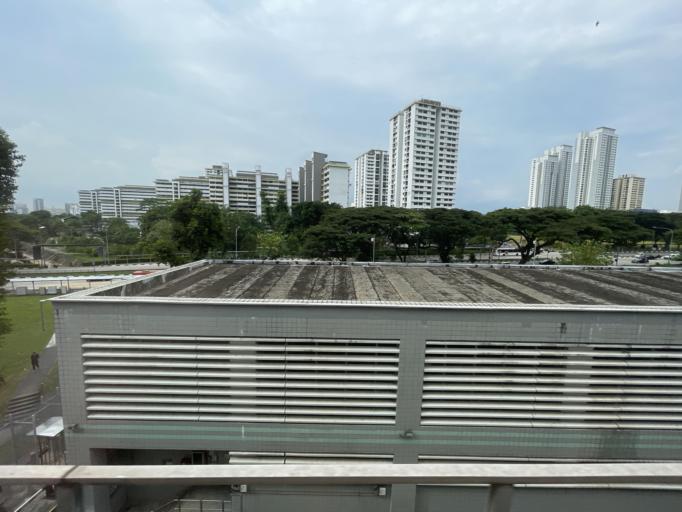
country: SG
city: Singapore
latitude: 1.3076
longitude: 103.7886
